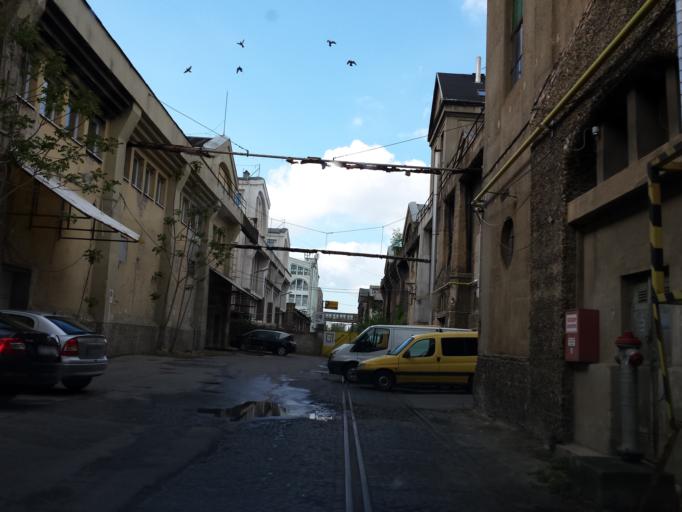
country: HU
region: Budapest
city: Budapest XX. keruelet
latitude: 47.4460
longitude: 19.0937
